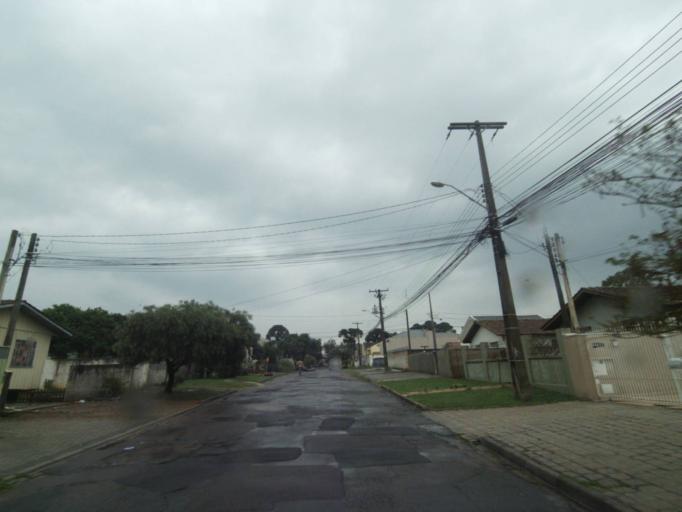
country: BR
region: Parana
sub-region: Curitiba
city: Curitiba
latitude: -25.4743
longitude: -49.3139
